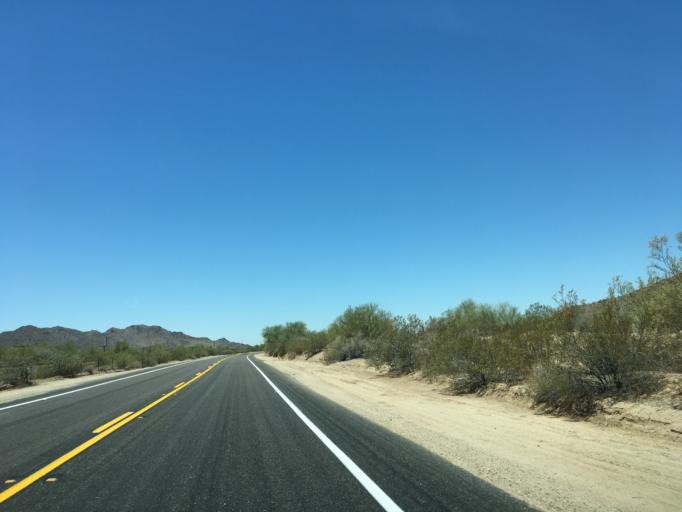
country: US
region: Arizona
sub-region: Maricopa County
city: Gila Bend
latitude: 32.9952
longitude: -112.4344
